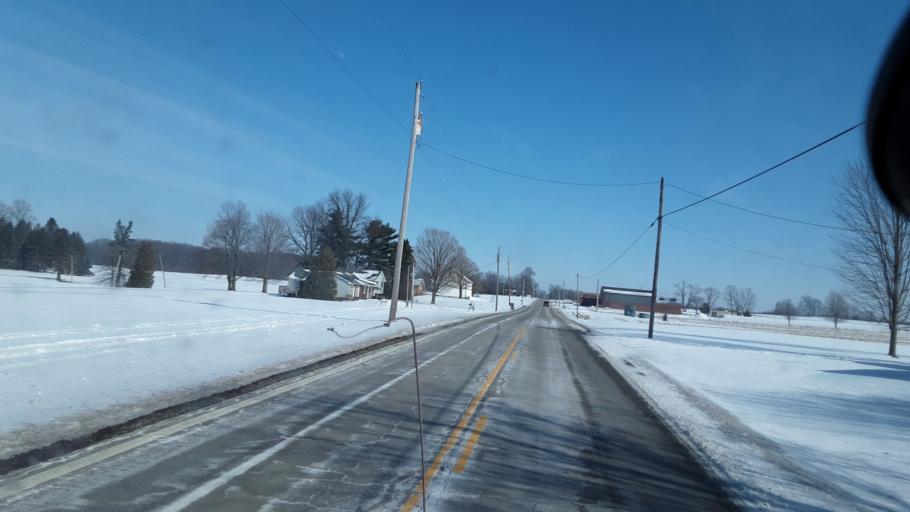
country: US
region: Ohio
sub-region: Columbiana County
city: Salem
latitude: 40.9448
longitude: -80.9205
